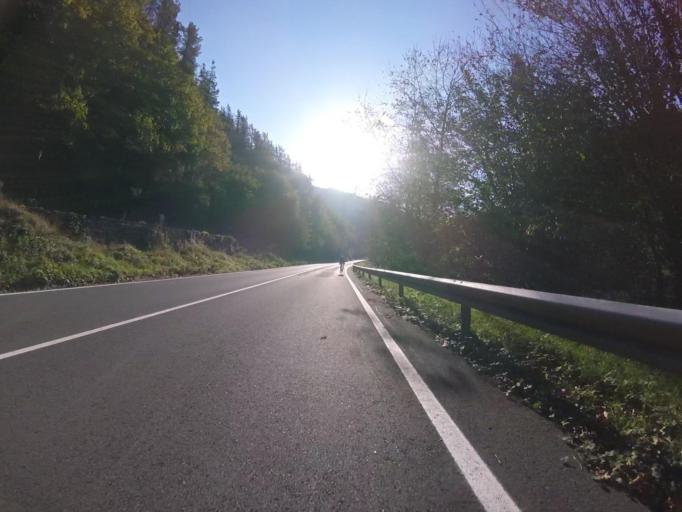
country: ES
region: Navarre
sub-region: Provincia de Navarra
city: Lesaka
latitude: 43.2504
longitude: -1.6725
